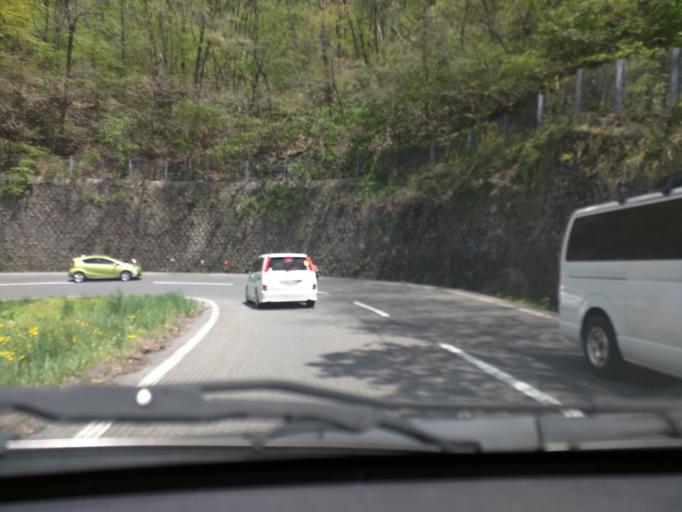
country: JP
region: Nagano
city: Nagano-shi
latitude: 36.6947
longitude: 138.1528
